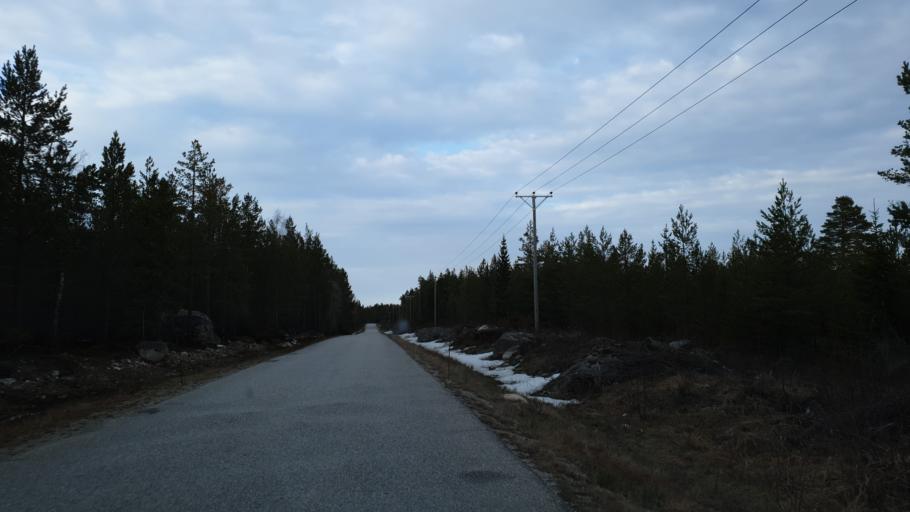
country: SE
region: Vaesternorrland
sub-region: Sundsvalls Kommun
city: Njurundabommen
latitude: 61.9927
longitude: 17.3813
